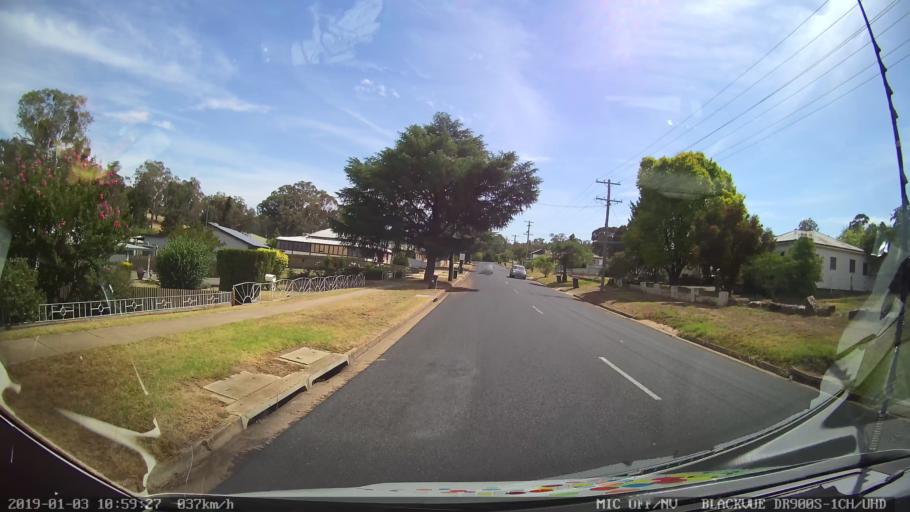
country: AU
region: New South Wales
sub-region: Young
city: Young
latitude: -34.3077
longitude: 148.2989
